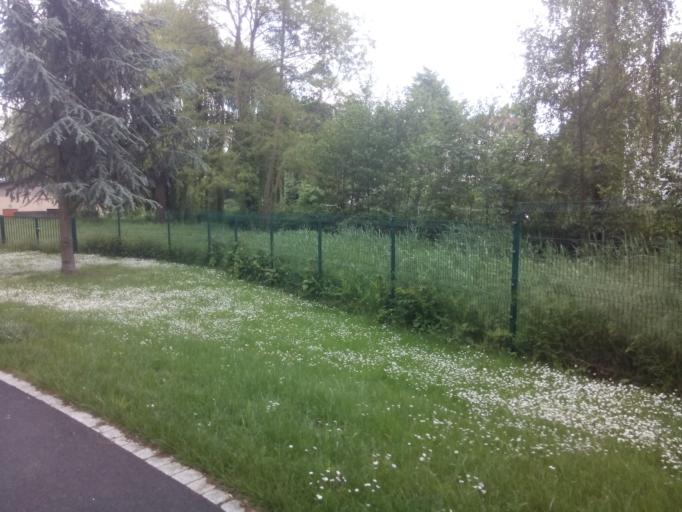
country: FR
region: Alsace
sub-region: Departement du Bas-Rhin
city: Bischwiller
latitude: 48.7715
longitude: 7.8499
